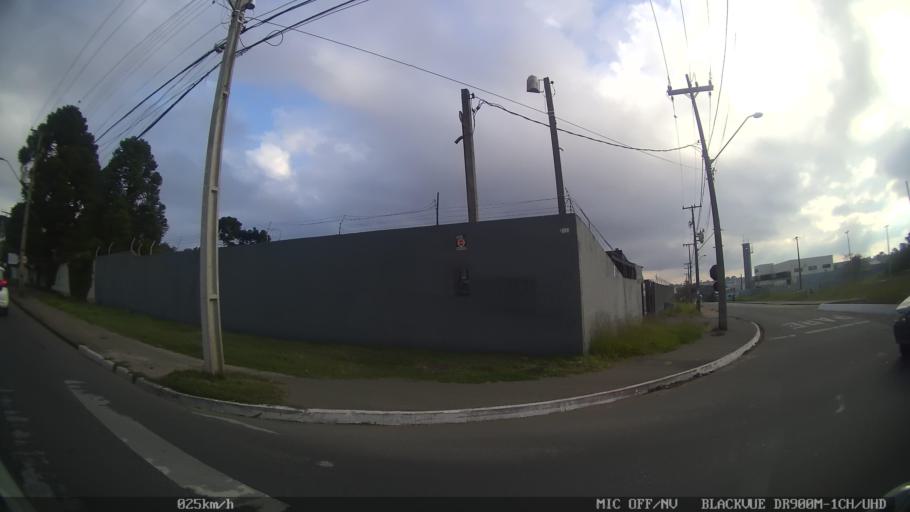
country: BR
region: Parana
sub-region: Pinhais
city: Pinhais
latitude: -25.4124
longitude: -49.1813
